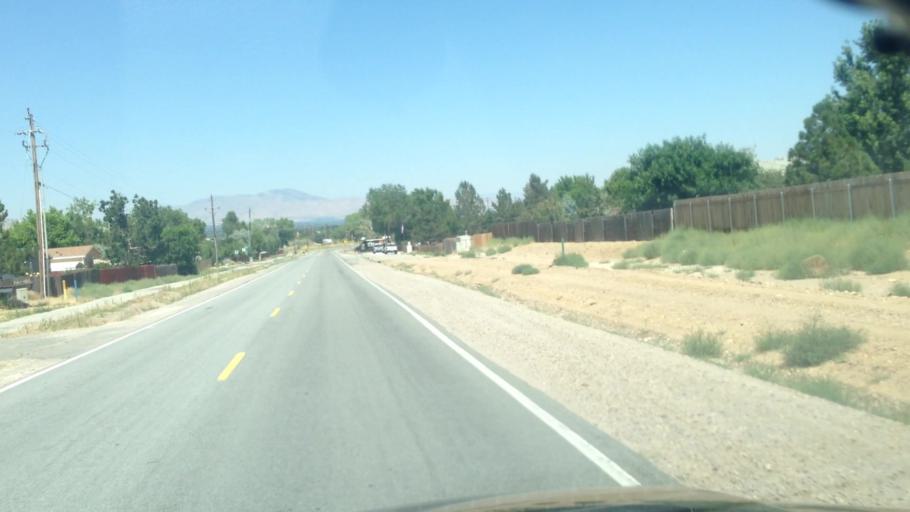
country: US
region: Nevada
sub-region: Storey County
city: Virginia City
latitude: 39.3939
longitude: -119.7332
